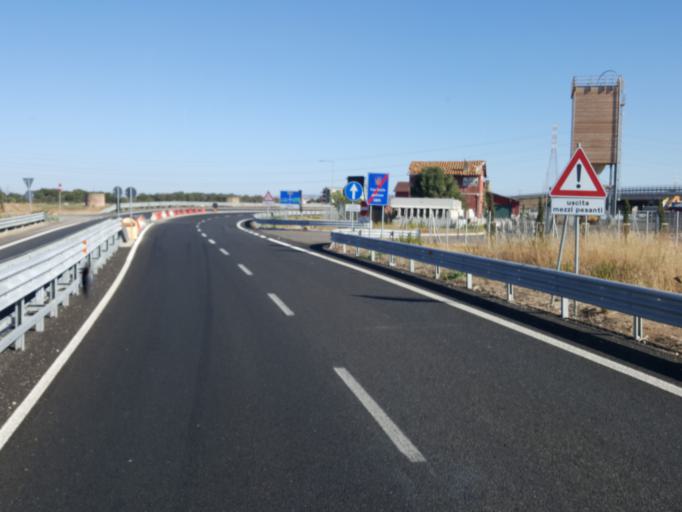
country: IT
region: Latium
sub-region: Citta metropolitana di Roma Capitale
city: Aurelia
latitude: 42.1619
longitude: 11.7884
